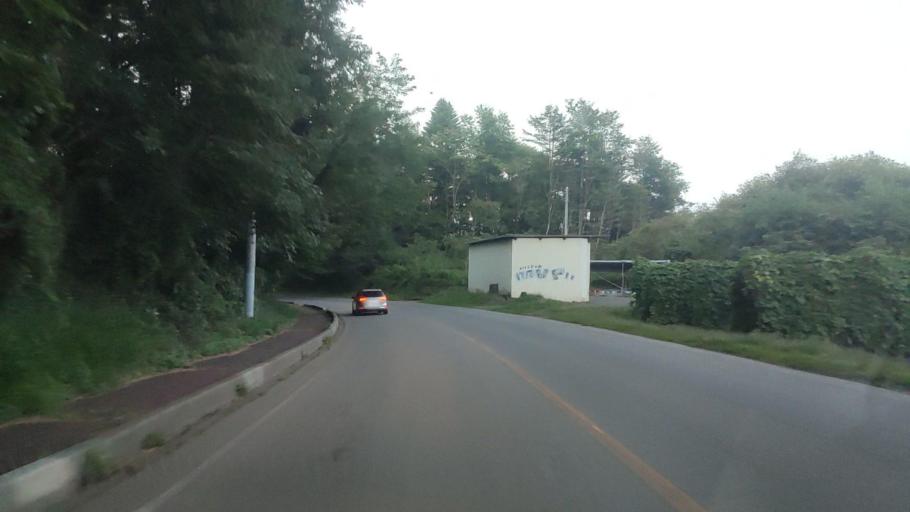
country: JP
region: Gunma
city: Nakanojomachi
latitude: 36.5145
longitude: 138.5987
